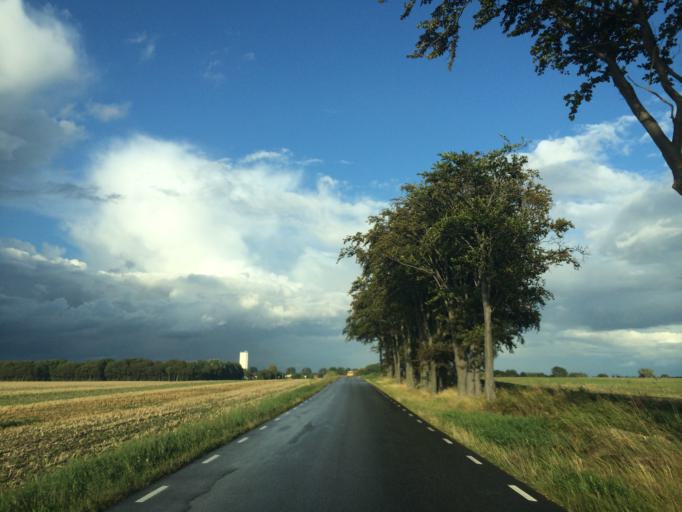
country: SE
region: Skane
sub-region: Kavlinge Kommun
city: Hofterup
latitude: 55.7718
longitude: 12.9372
